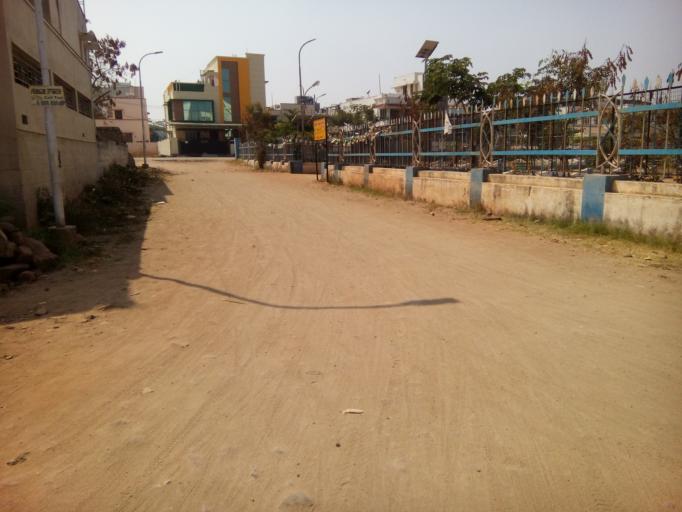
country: IN
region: Tamil Nadu
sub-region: Coimbatore
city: Singanallur
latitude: 11.0035
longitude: 77.0315
